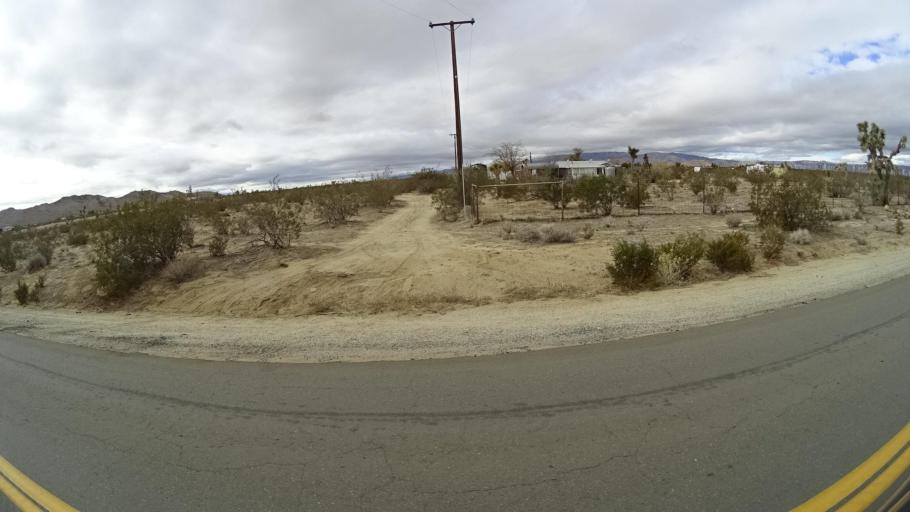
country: US
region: California
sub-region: Kern County
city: Rosamond
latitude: 34.9471
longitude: -118.2126
